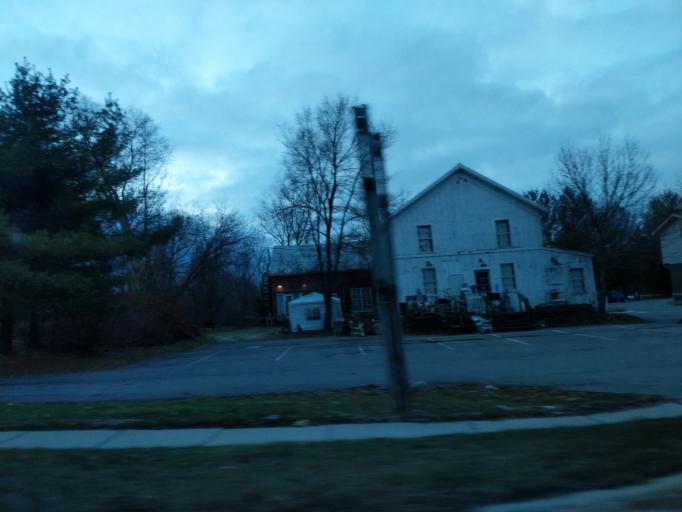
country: US
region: Michigan
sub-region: Lapeer County
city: Almont
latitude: 42.9158
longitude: -83.0449
